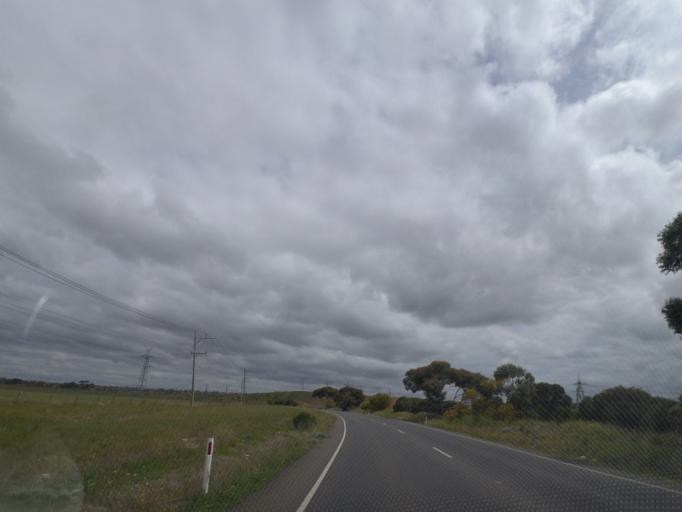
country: AU
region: Victoria
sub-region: Brimbank
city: Sydenham
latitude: -37.6763
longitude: 144.7665
